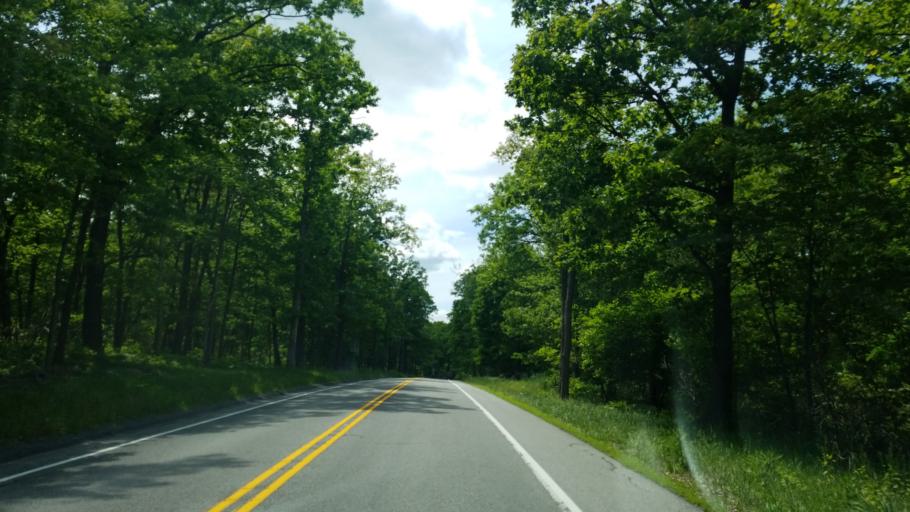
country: US
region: Pennsylvania
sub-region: Blair County
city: Tipton
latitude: 40.7012
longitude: -78.2994
